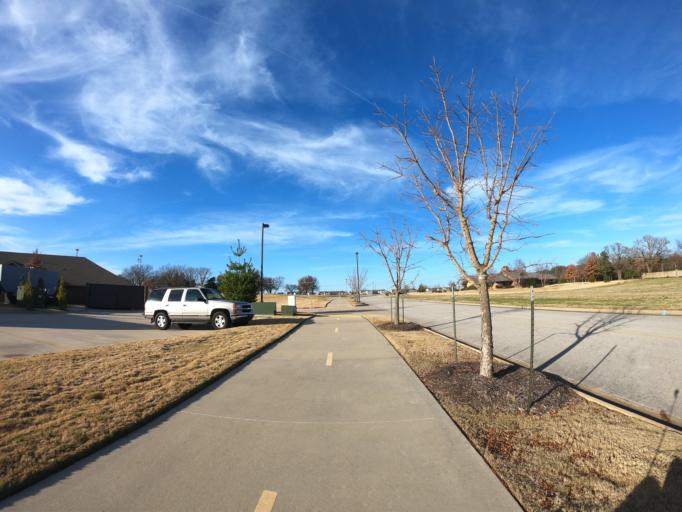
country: US
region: Arkansas
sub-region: Benton County
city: Bentonville
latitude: 36.3259
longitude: -94.1762
